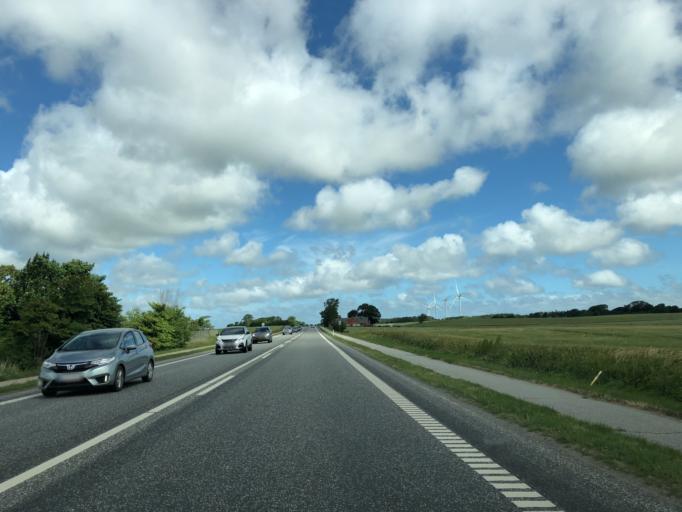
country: DK
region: Central Jutland
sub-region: Holstebro Kommune
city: Holstebro
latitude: 56.4049
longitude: 8.6062
